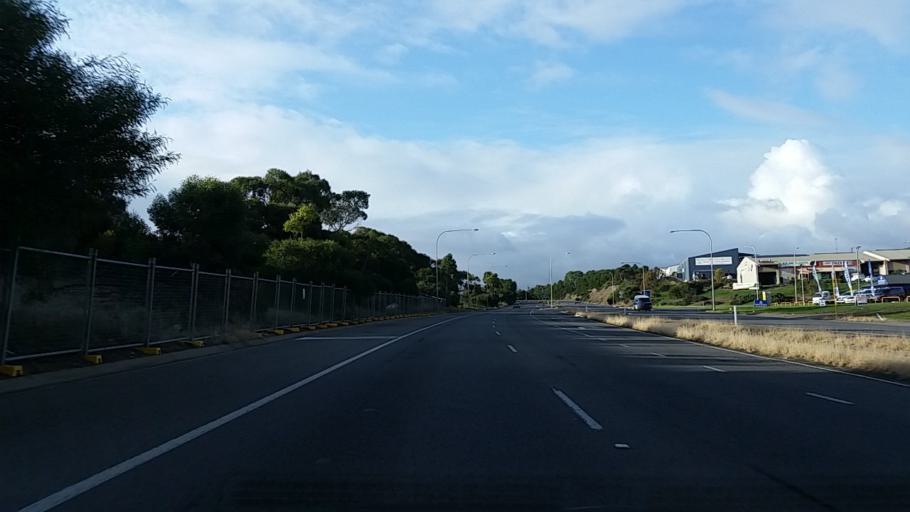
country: AU
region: South Australia
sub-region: Onkaparinga
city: Morphett Vale
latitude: -35.1109
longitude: 138.4936
